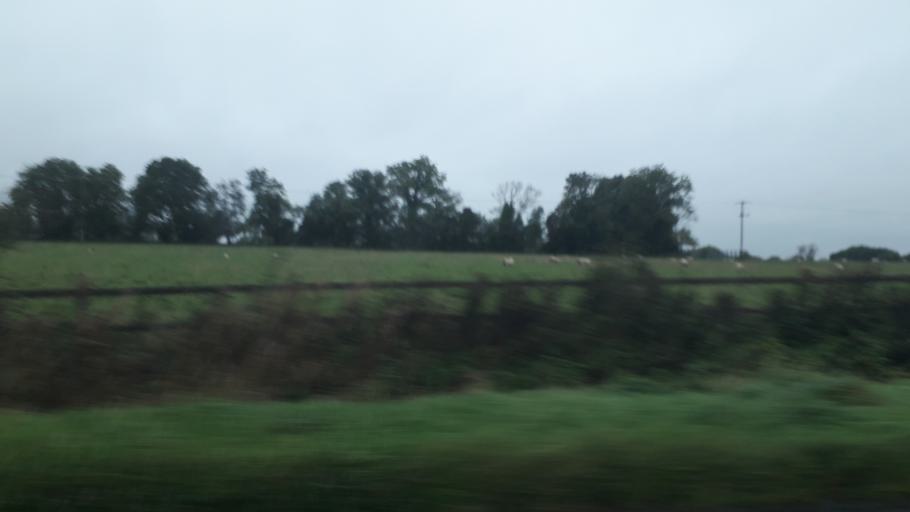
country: IE
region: Leinster
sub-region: An Longfort
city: Granard
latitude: 53.6417
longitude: -7.4983
